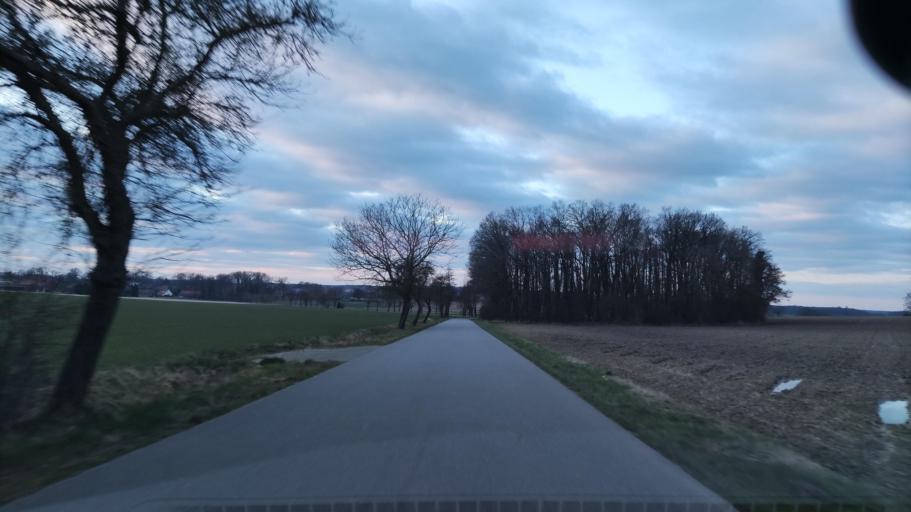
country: DE
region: Lower Saxony
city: Natendorf
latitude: 53.0528
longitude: 10.4666
